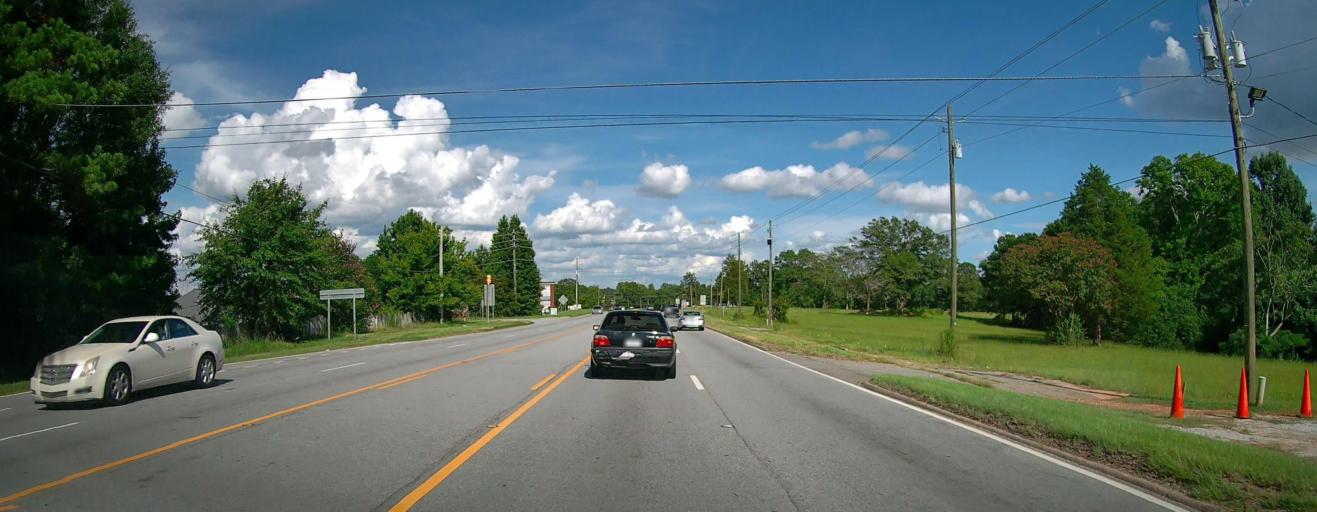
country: US
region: Alabama
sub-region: Russell County
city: Ladonia
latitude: 32.4691
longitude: -85.0828
